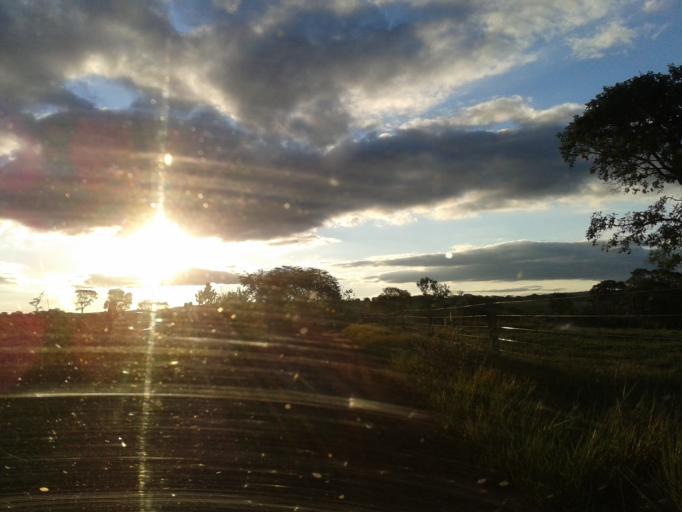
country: BR
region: Minas Gerais
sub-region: Campina Verde
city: Campina Verde
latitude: -19.5057
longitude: -49.6831
